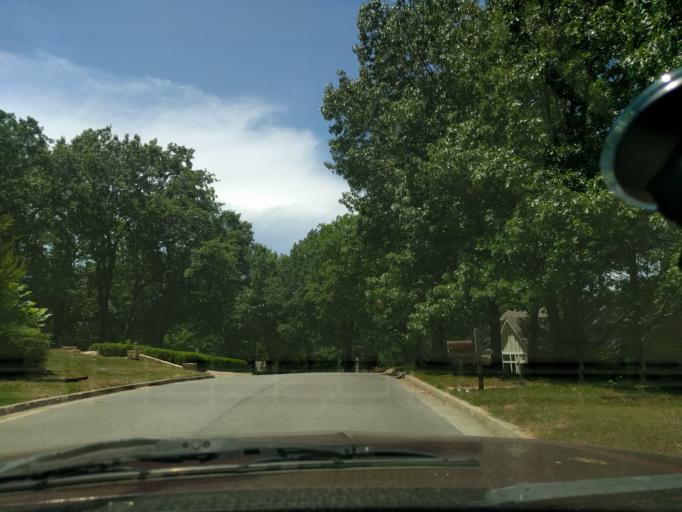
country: US
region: Oklahoma
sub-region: Tulsa County
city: Jenks
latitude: 36.0196
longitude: -95.9346
